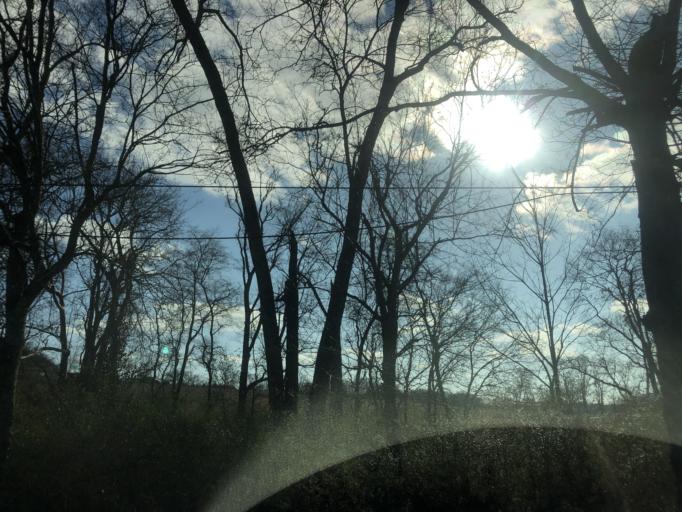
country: US
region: Tennessee
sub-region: Sumner County
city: Shackle Island
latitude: 36.3557
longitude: -86.5385
